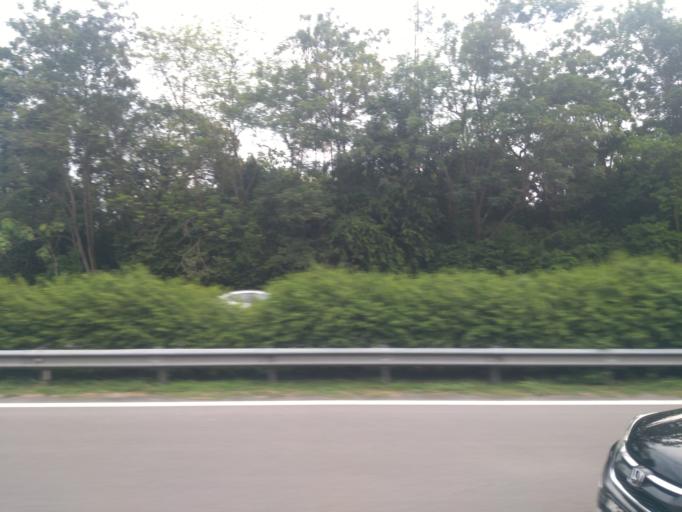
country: MY
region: Melaka
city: Alor Gajah
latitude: 2.3609
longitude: 102.2512
